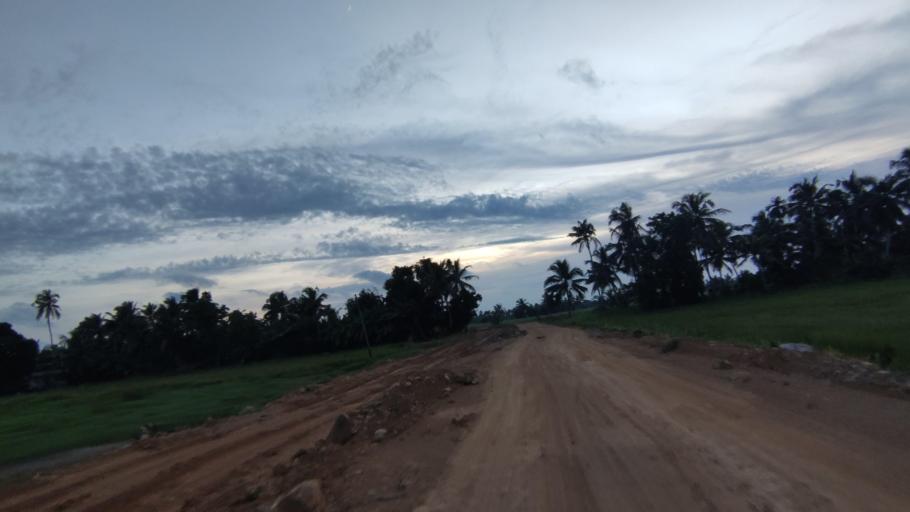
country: IN
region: Kerala
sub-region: Kottayam
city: Kottayam
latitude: 9.6459
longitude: 76.4587
